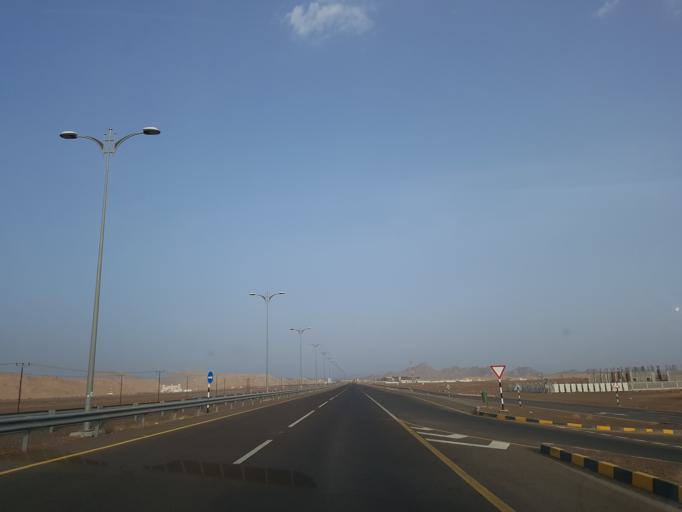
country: OM
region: Al Buraimi
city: Al Buraymi
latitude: 24.2350
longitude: 55.9180
